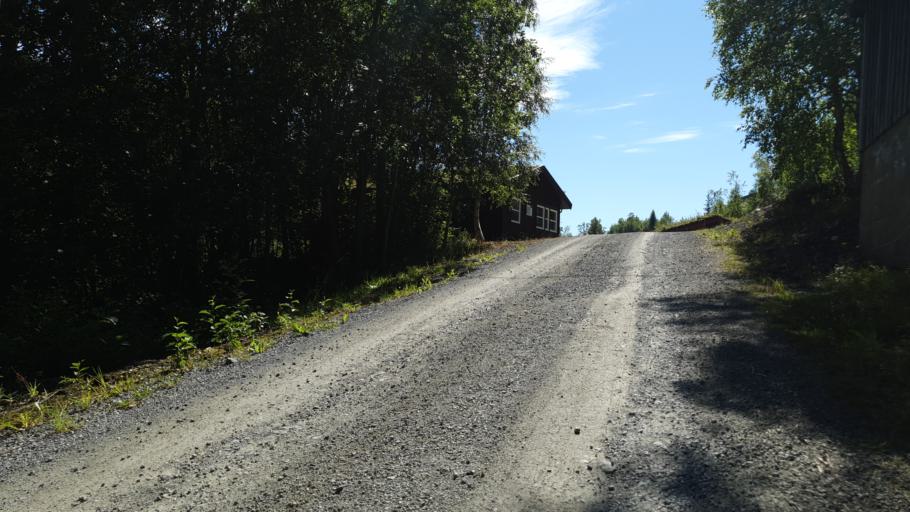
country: NO
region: Sor-Trondelag
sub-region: Meldal
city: Meldal
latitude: 63.1225
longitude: 9.7016
